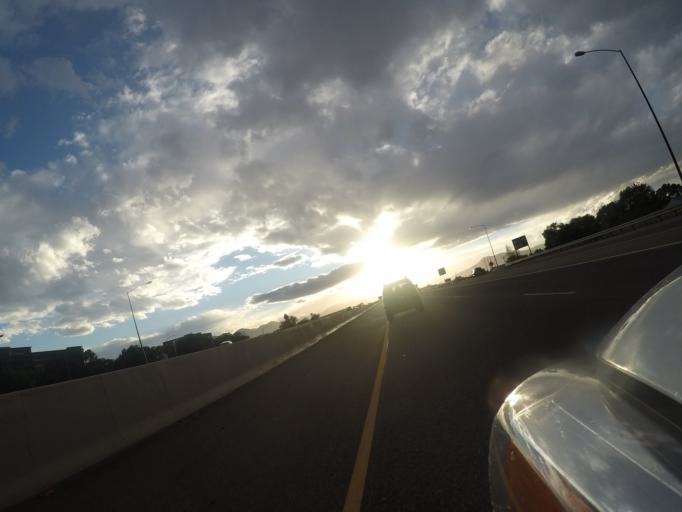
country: US
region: Colorado
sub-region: Jefferson County
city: Lakewood
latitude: 39.6530
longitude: -105.0779
